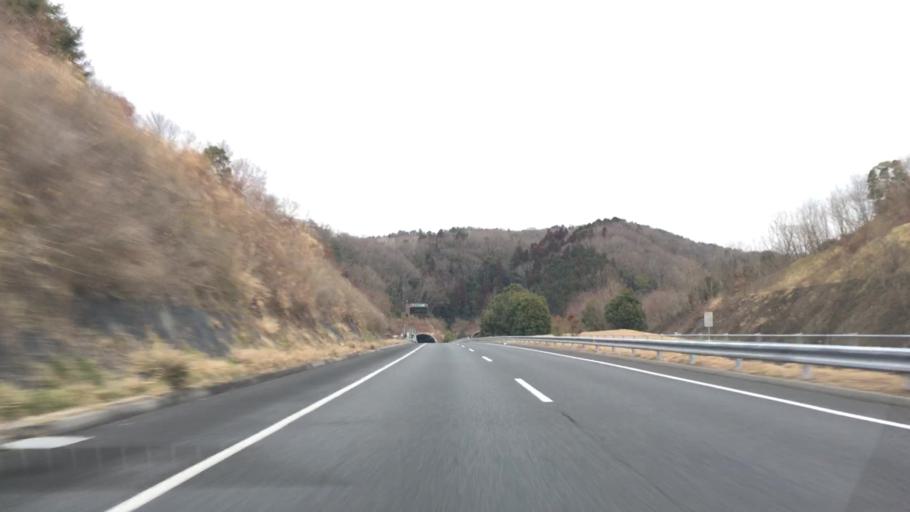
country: JP
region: Aichi
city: Seto
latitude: 35.2584
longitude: 137.1505
